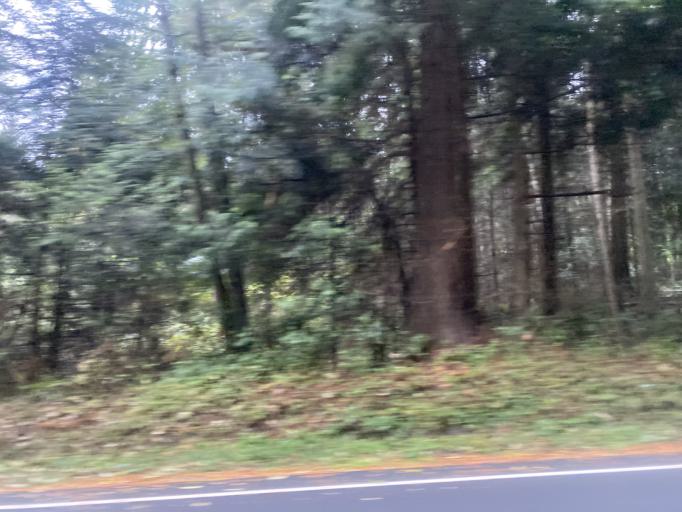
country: US
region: Washington
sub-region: Island County
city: Freeland
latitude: 48.0747
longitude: -122.4850
